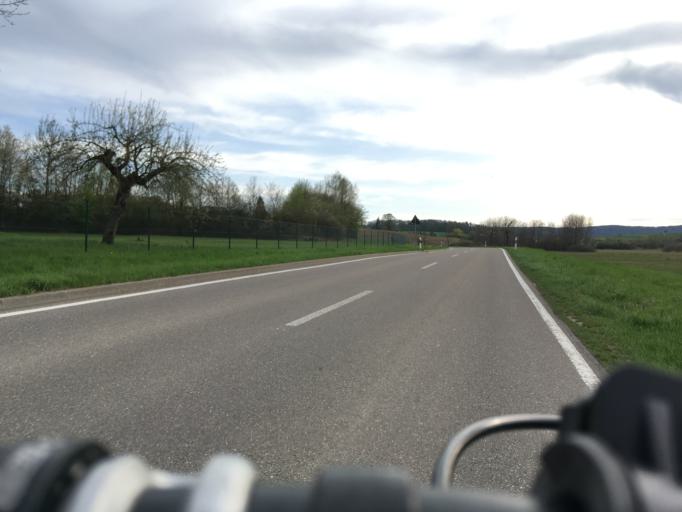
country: CH
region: Schaffhausen
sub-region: Bezirk Reiat
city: Thayngen
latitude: 47.8003
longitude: 8.7273
